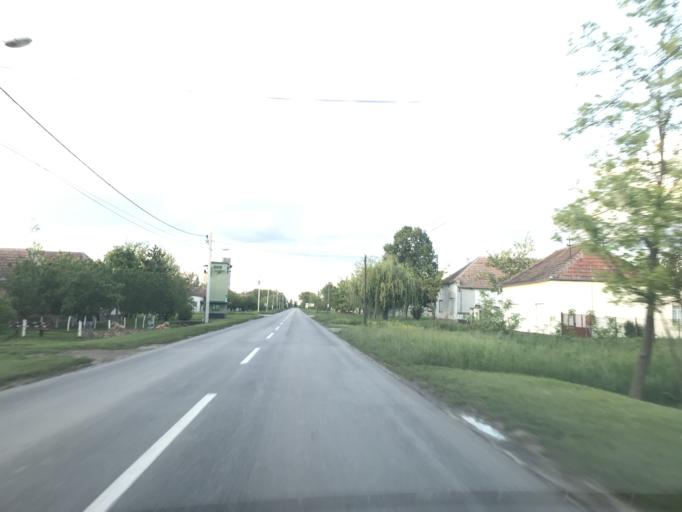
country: RS
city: Cestereg
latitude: 45.5651
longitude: 20.5344
